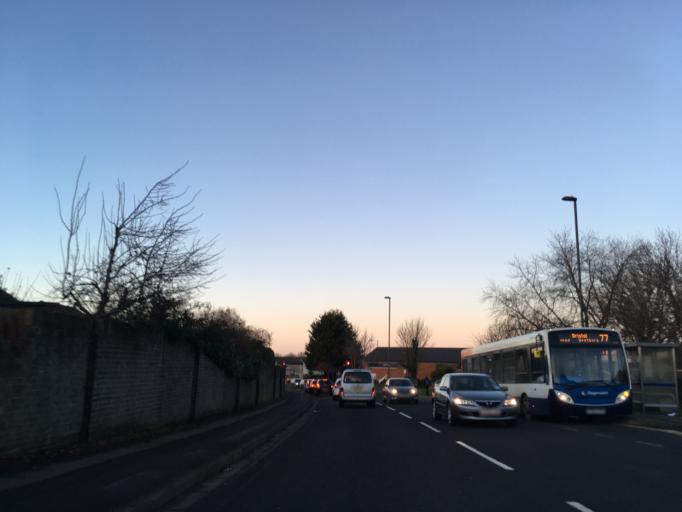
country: GB
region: England
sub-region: South Gloucestershire
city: Stoke Gifford
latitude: 51.5164
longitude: -2.5467
